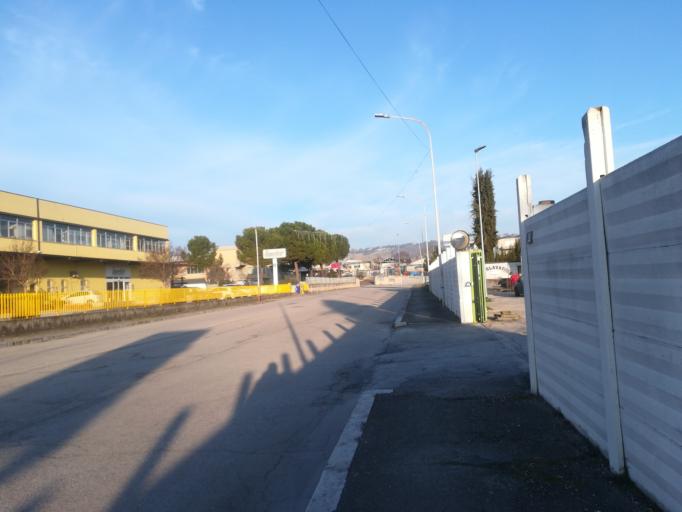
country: IT
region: The Marches
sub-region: Provincia di Macerata
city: Piediripa
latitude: 43.2778
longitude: 13.4945
